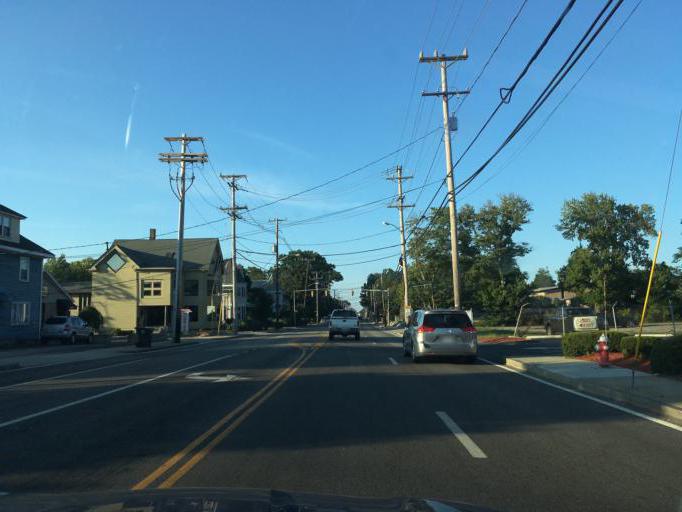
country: US
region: Rhode Island
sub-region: Kent County
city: Warwick
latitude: 41.7297
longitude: -71.4427
